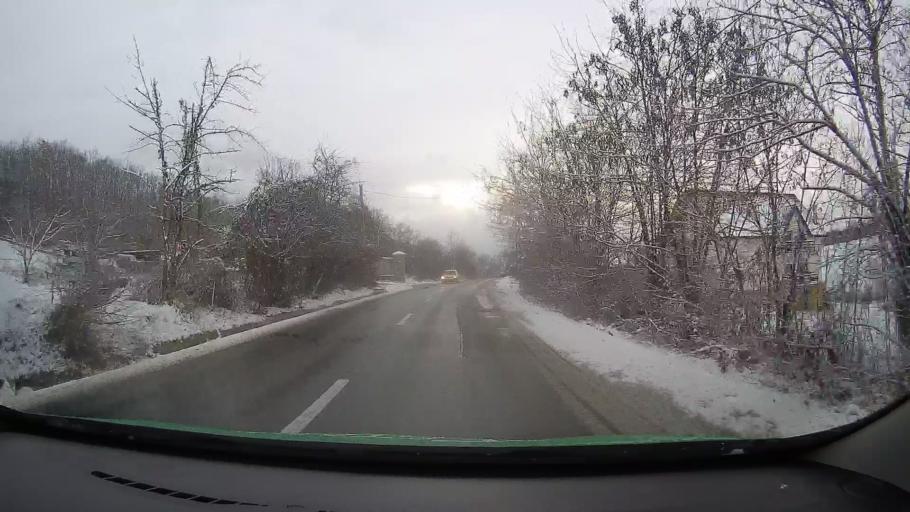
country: RO
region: Hunedoara
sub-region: Oras Hateg
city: Hateg
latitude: 45.6297
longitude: 22.9307
